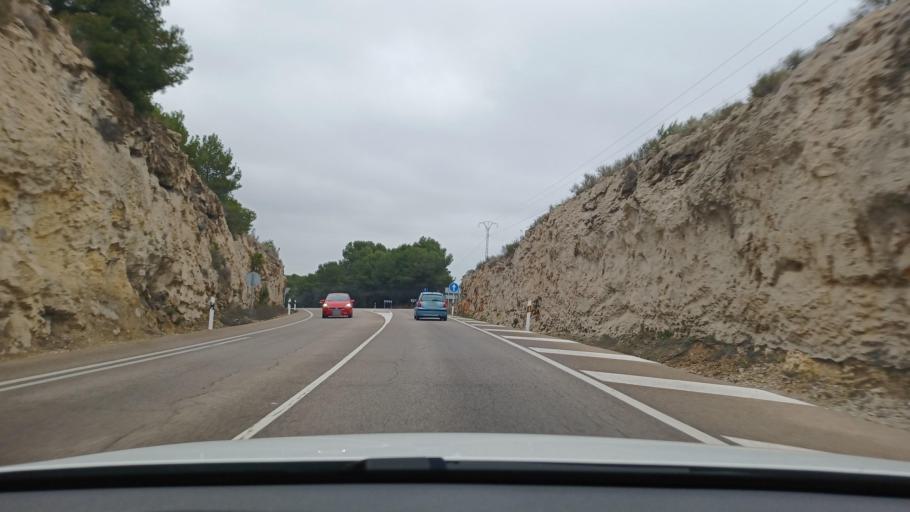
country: ES
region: Valencia
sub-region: Provincia de Castello
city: Benicassim
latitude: 40.0720
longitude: 0.1087
